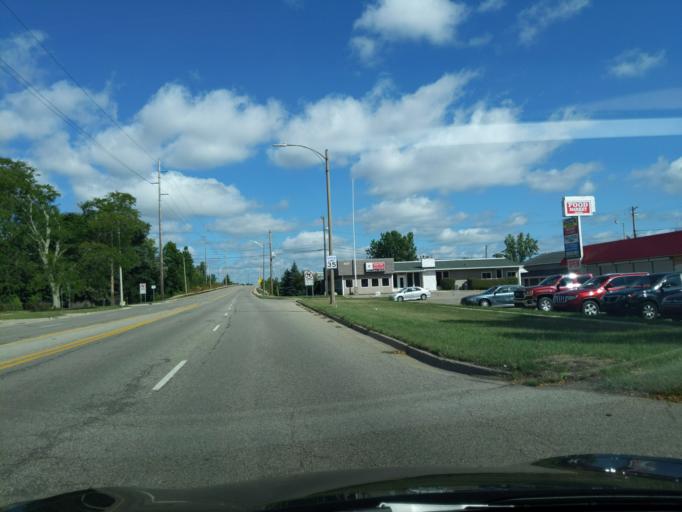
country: US
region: Michigan
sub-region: Ingham County
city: Lansing
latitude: 42.6996
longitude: -84.5379
